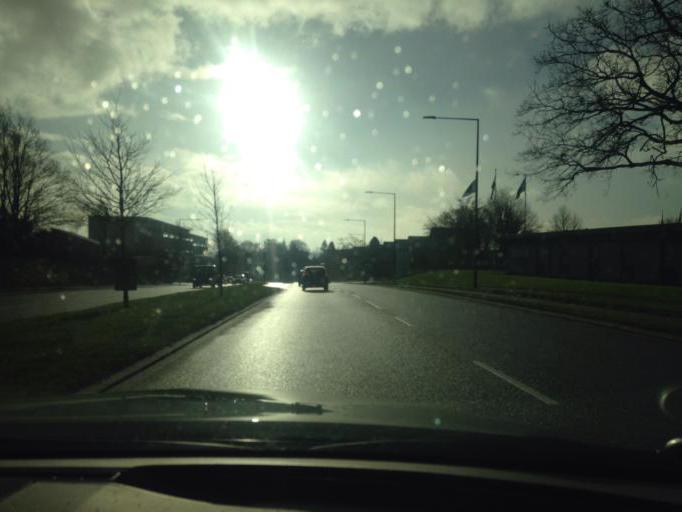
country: DK
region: South Denmark
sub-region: Kolding Kommune
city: Kolding
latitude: 55.5001
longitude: 9.4572
